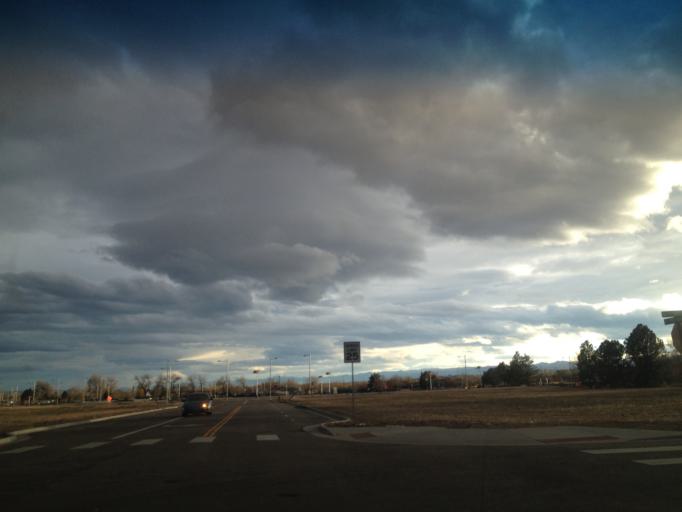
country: US
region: Colorado
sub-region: Adams County
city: Westminster
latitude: 39.8614
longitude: -105.0627
